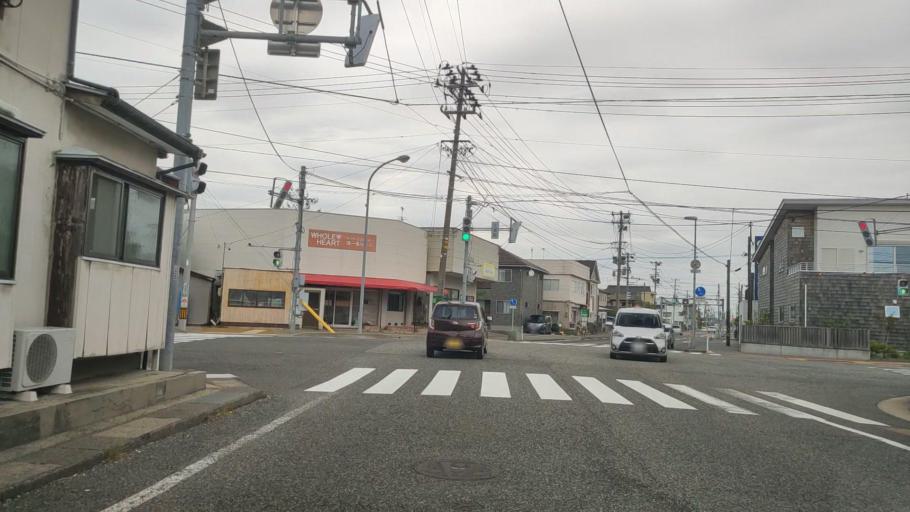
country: JP
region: Niigata
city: Niigata-shi
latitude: 37.9386
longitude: 139.0741
